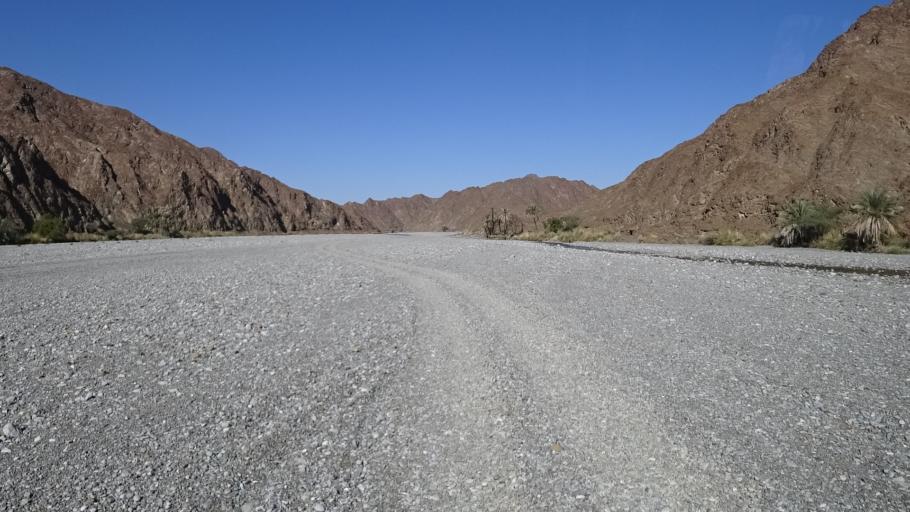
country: OM
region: Al Batinah
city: Bayt al `Awabi
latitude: 23.4050
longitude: 57.6661
